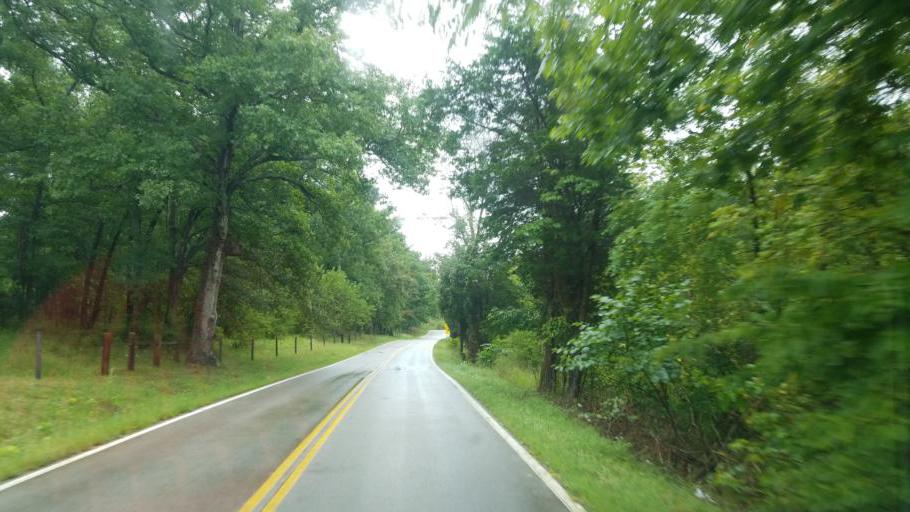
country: US
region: Ohio
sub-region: Adams County
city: West Union
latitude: 38.7813
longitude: -83.5374
